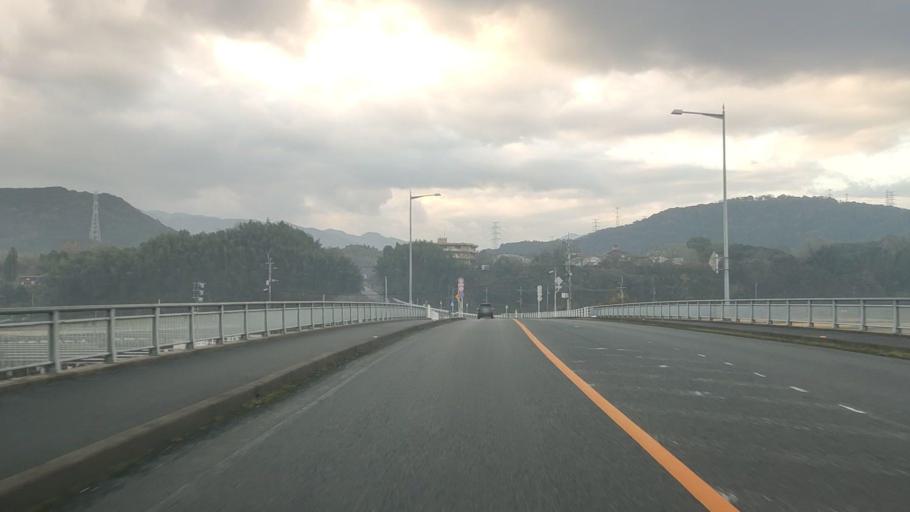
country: JP
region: Kumamoto
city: Matsubase
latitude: 32.6423
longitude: 130.8130
